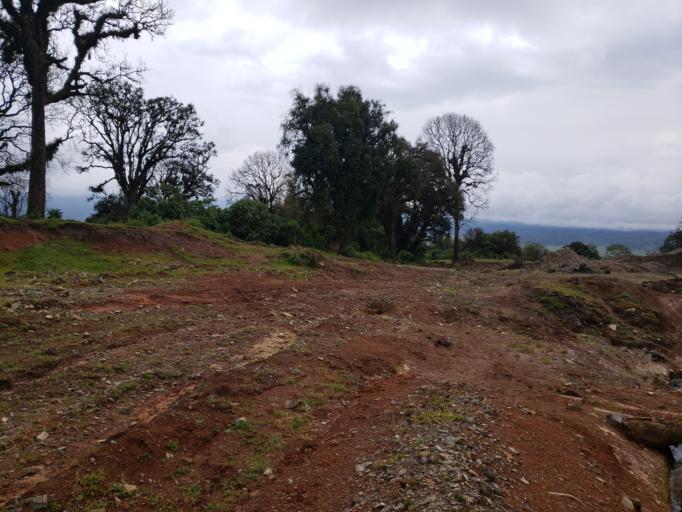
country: ET
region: Oromiya
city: Dodola
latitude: 6.6496
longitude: 39.3667
